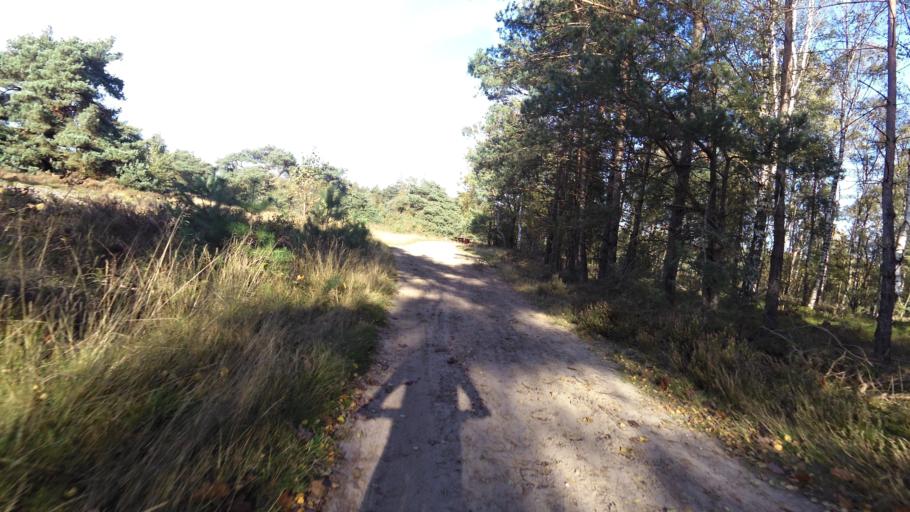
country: NL
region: Gelderland
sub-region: Gemeente Epe
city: Epe
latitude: 52.3757
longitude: 5.9941
